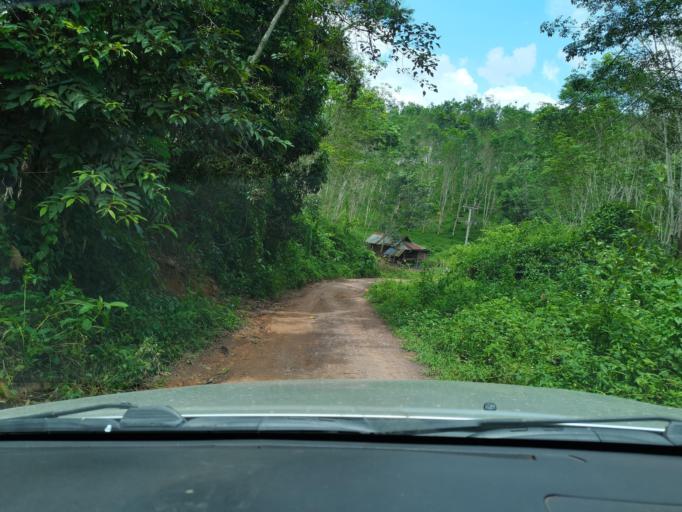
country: LA
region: Loungnamtha
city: Muang Long
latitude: 20.7010
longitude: 101.0280
